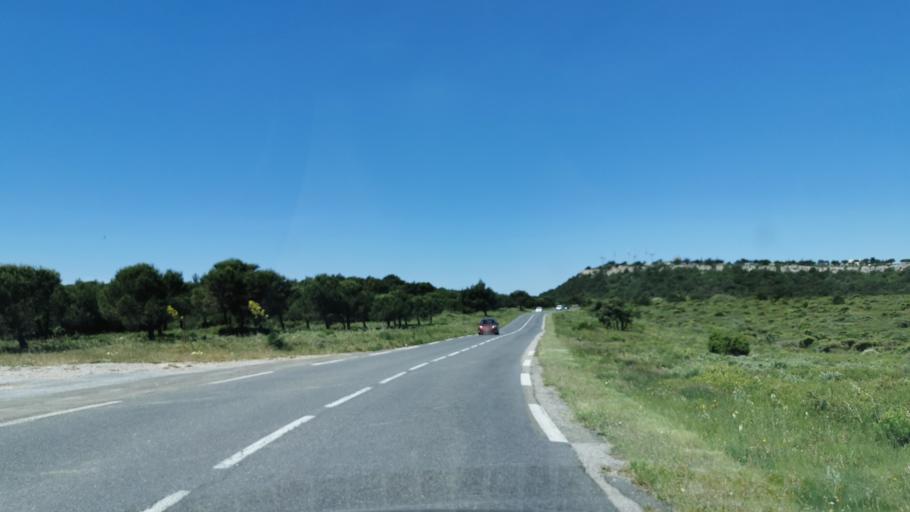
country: FR
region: Languedoc-Roussillon
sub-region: Departement de l'Aude
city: Armissan
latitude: 43.1693
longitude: 3.1297
